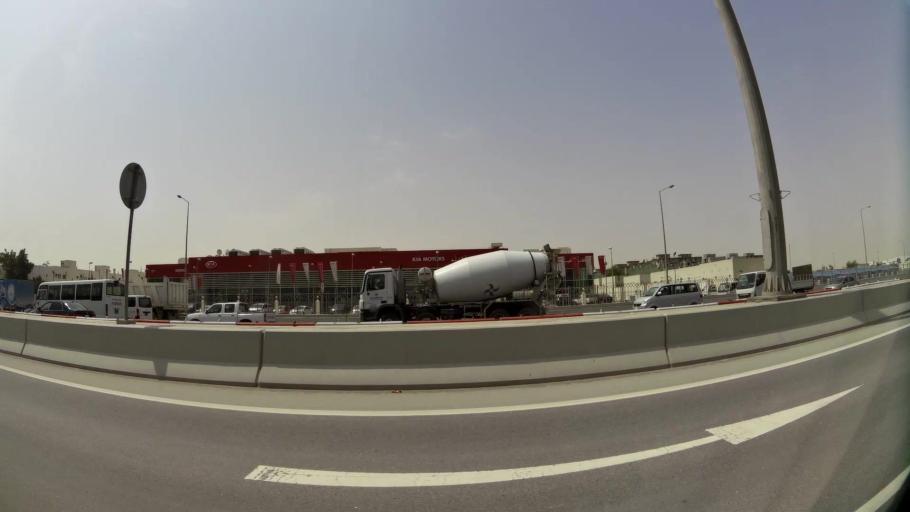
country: QA
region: Baladiyat ar Rayyan
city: Ar Rayyan
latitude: 25.1989
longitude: 51.4509
